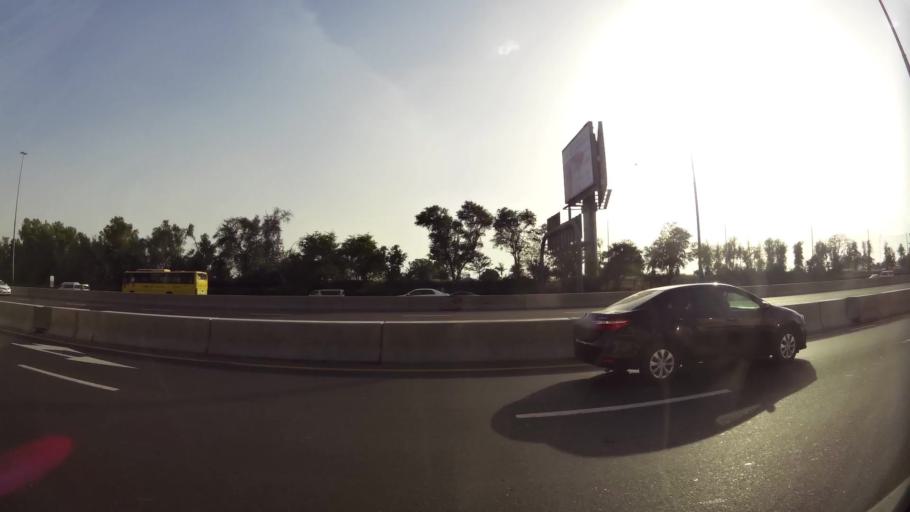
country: AE
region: Ash Shariqah
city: Sharjah
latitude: 25.2441
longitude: 55.3390
